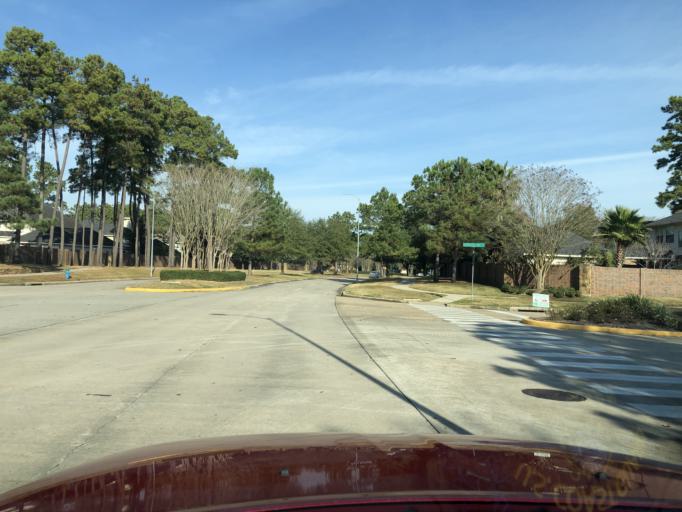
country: US
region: Texas
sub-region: Harris County
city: Tomball
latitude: 30.0315
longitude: -95.5666
